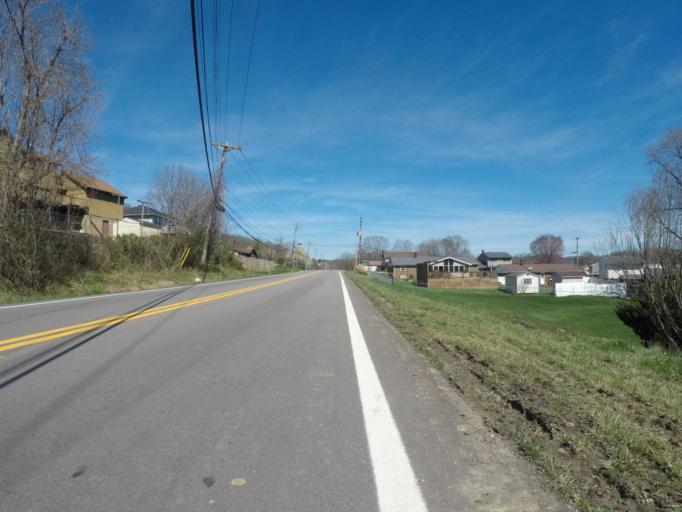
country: US
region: West Virginia
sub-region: Cabell County
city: Pea Ridge
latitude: 38.3994
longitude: -82.3200
